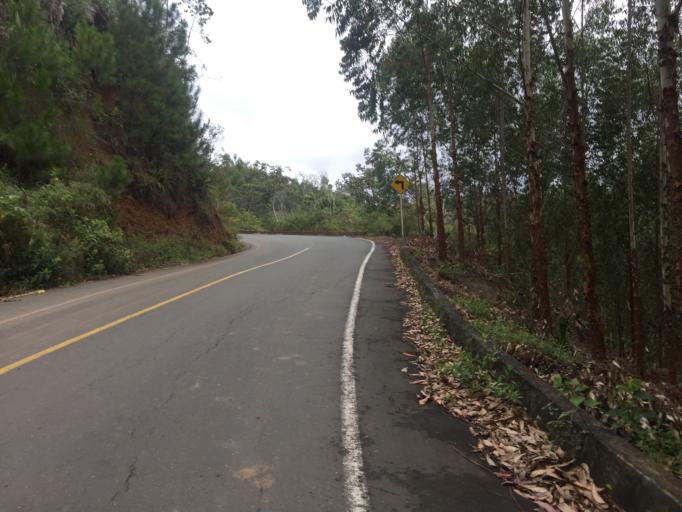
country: CO
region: Valle del Cauca
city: Dagua
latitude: 3.7065
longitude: -76.5868
